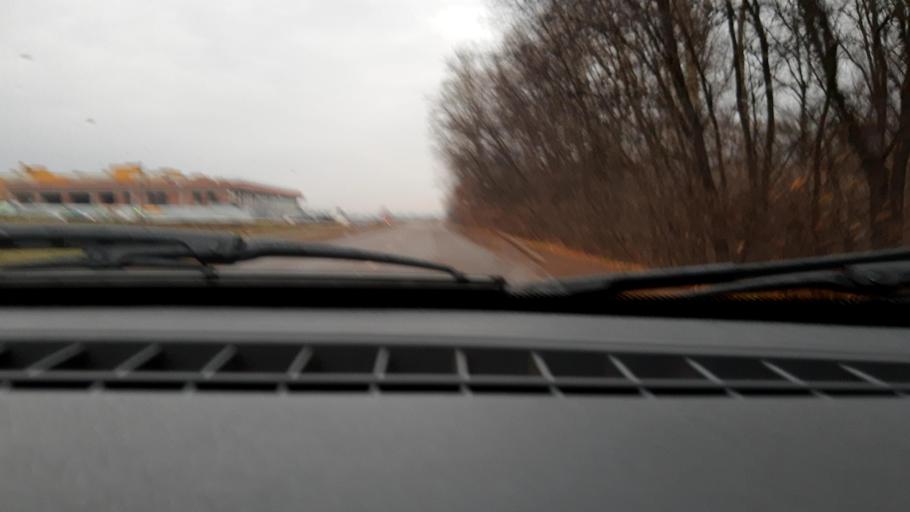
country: RU
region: Bashkortostan
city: Ufa
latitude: 54.7945
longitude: 55.9587
